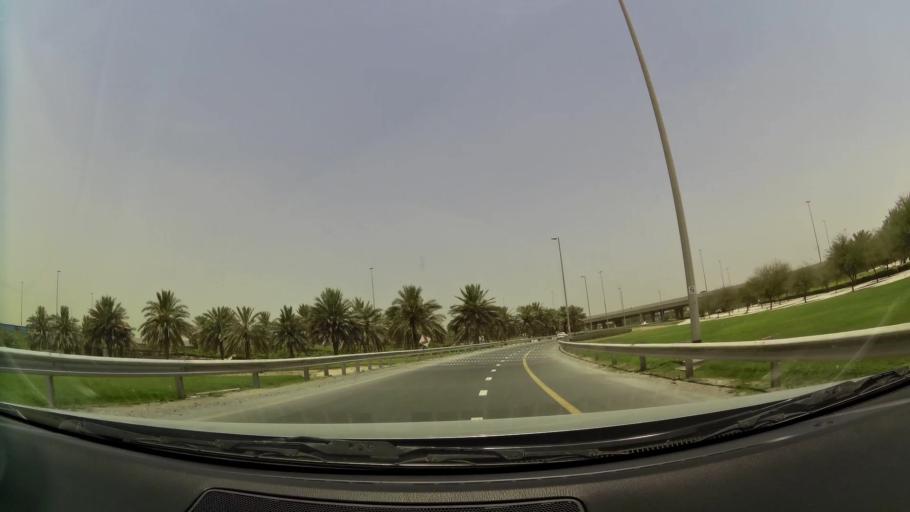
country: AE
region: Dubai
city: Dubai
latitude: 25.0569
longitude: 55.2506
